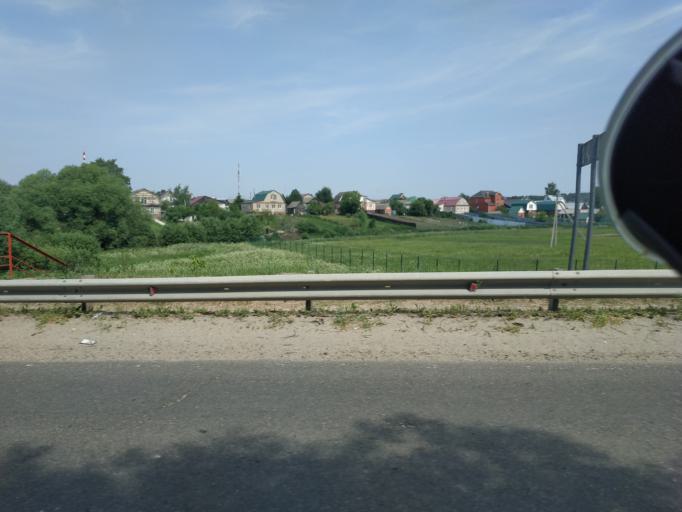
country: RU
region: Moskovskaya
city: Malyshevo
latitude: 55.5374
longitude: 38.3162
